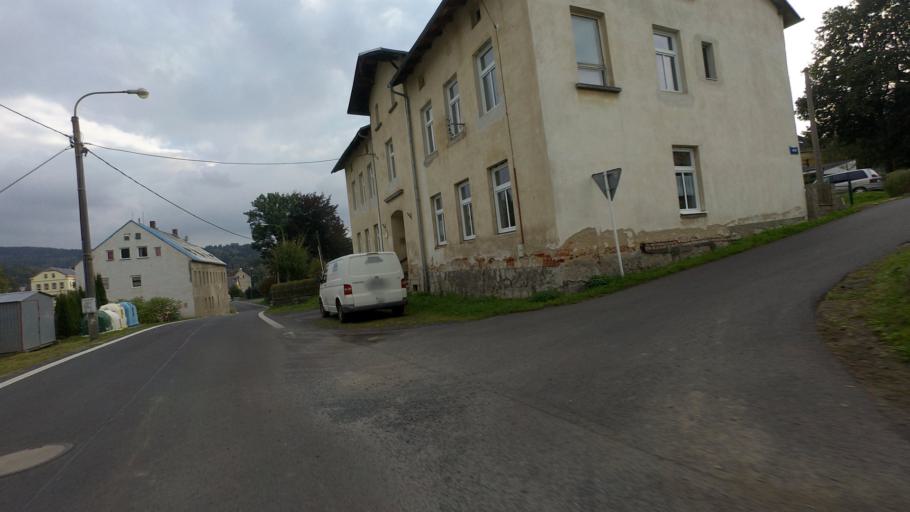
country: CZ
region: Ustecky
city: Dolni Poustevna
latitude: 50.9845
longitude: 14.2888
